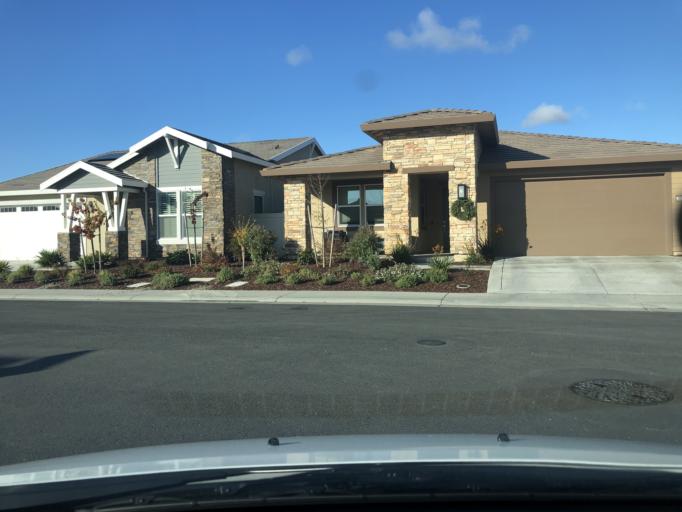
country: US
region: California
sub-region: Sacramento County
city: Antelope
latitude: 38.7747
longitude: -121.3880
